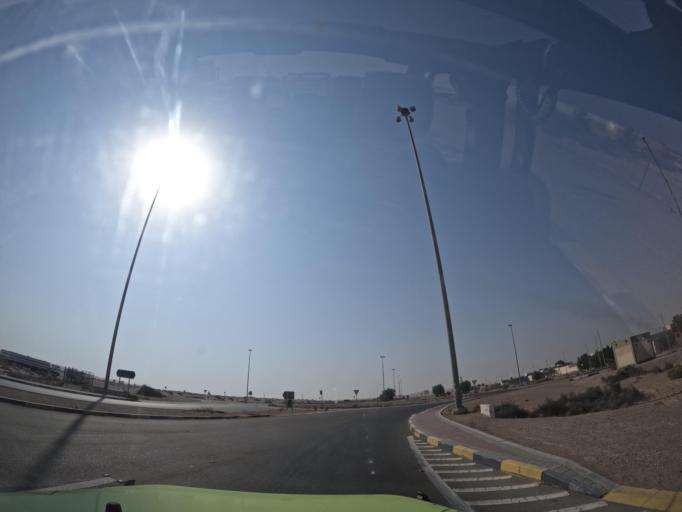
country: OM
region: Al Buraimi
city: Al Buraymi
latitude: 24.5251
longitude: 55.5528
